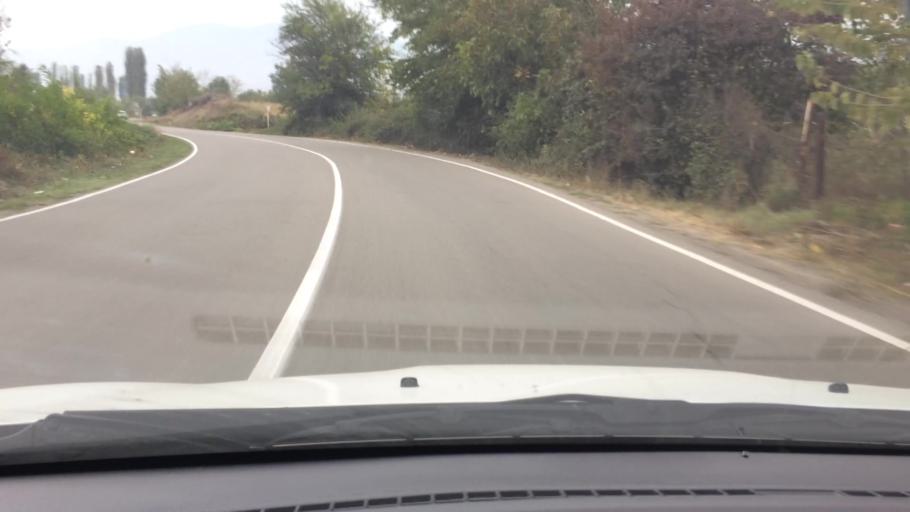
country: AM
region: Tavush
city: Bagratashen
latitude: 41.2590
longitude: 44.7963
